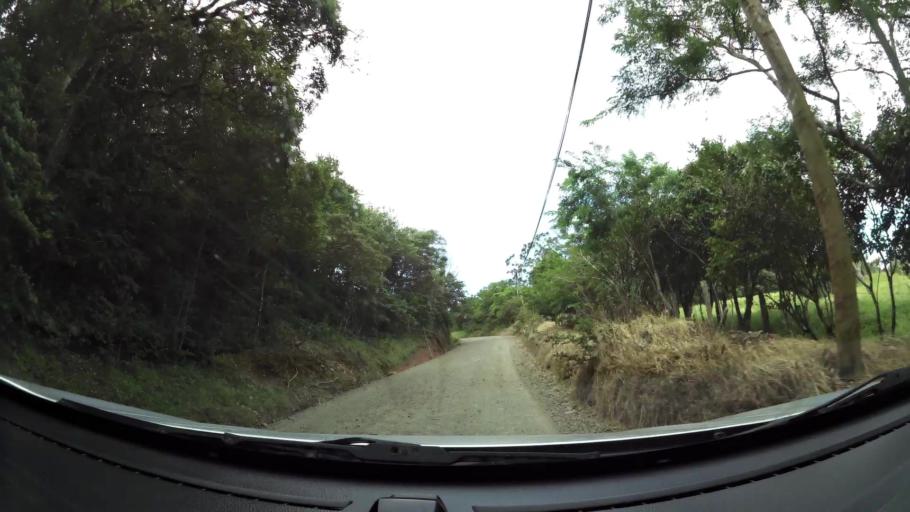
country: CR
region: Guanacaste
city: Juntas
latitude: 10.3508
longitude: -84.9091
